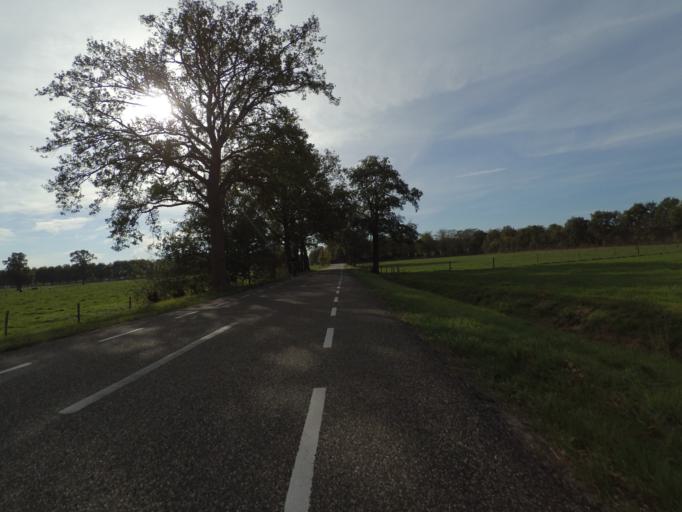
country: NL
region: Gelderland
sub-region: Gemeente Lochem
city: Laren
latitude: 52.2451
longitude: 6.3878
